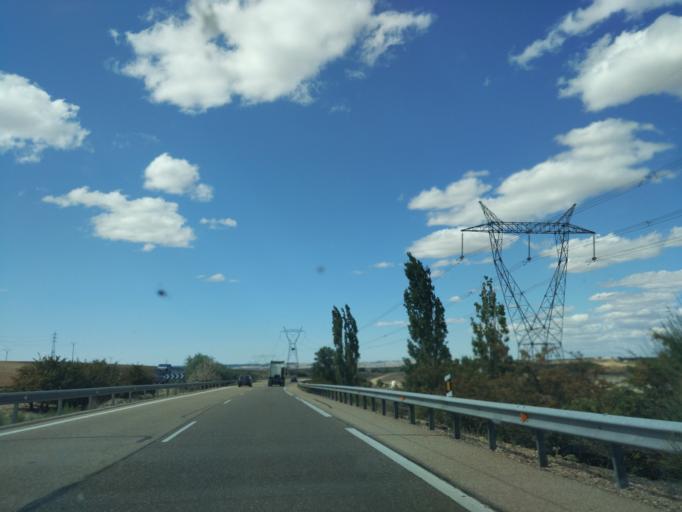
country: ES
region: Castille and Leon
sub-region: Provincia de Valladolid
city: Rueda
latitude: 41.4129
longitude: -4.9648
